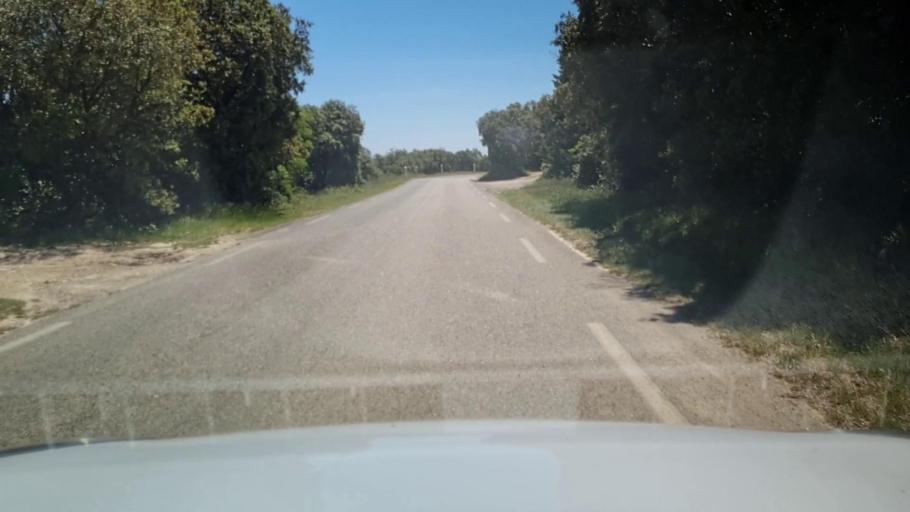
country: FR
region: Languedoc-Roussillon
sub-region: Departement du Gard
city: Clarensac
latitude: 43.8390
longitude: 4.2282
